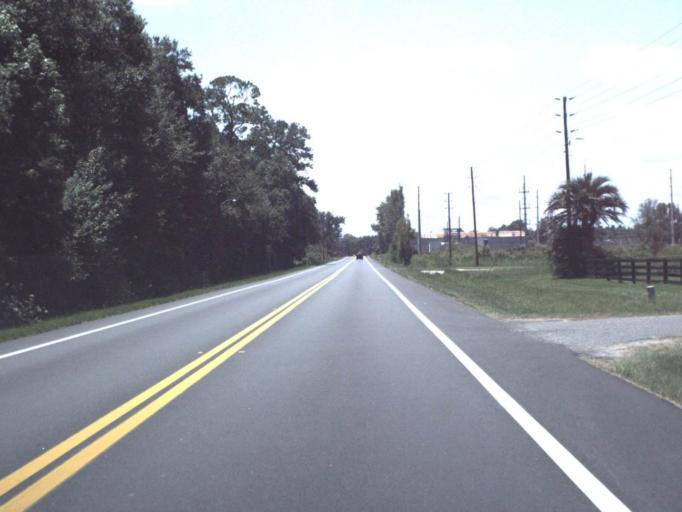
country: US
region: Florida
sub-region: Union County
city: Lake Butler
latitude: 29.9420
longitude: -82.4244
